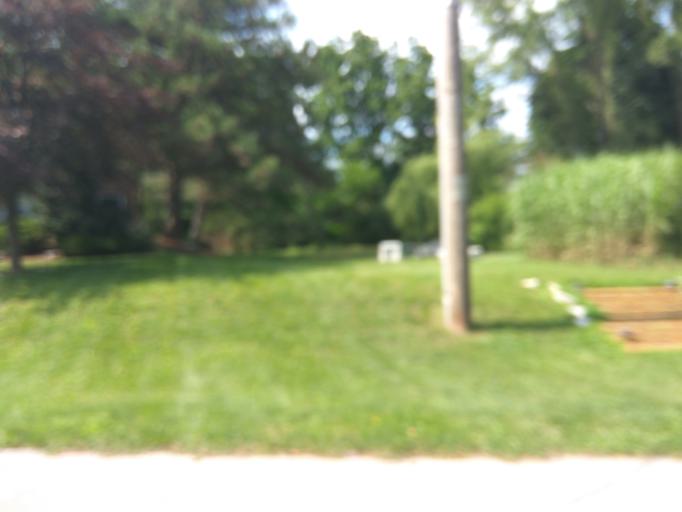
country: CA
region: Ontario
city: Cambridge
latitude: 43.4003
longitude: -80.3842
